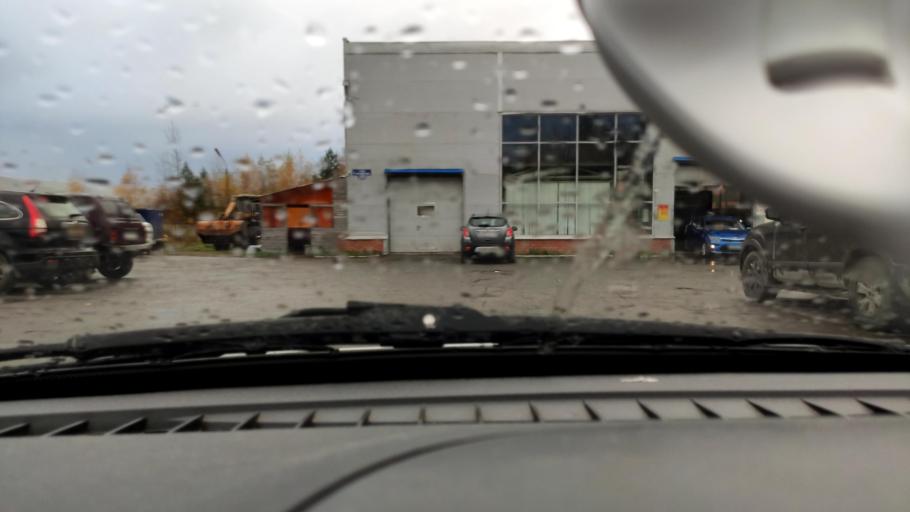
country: RU
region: Perm
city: Perm
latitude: 58.0386
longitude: 56.1841
